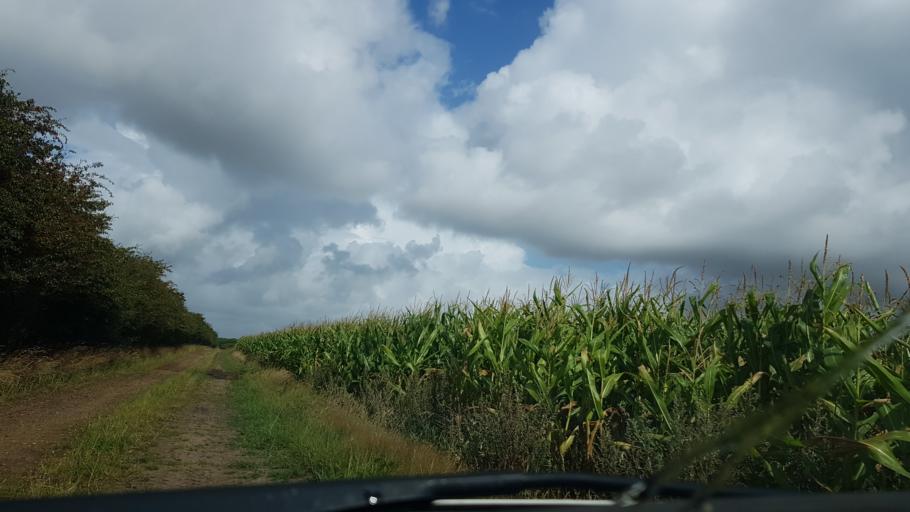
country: DK
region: South Denmark
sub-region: Esbjerg Kommune
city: Ribe
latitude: 55.2503
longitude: 8.7682
